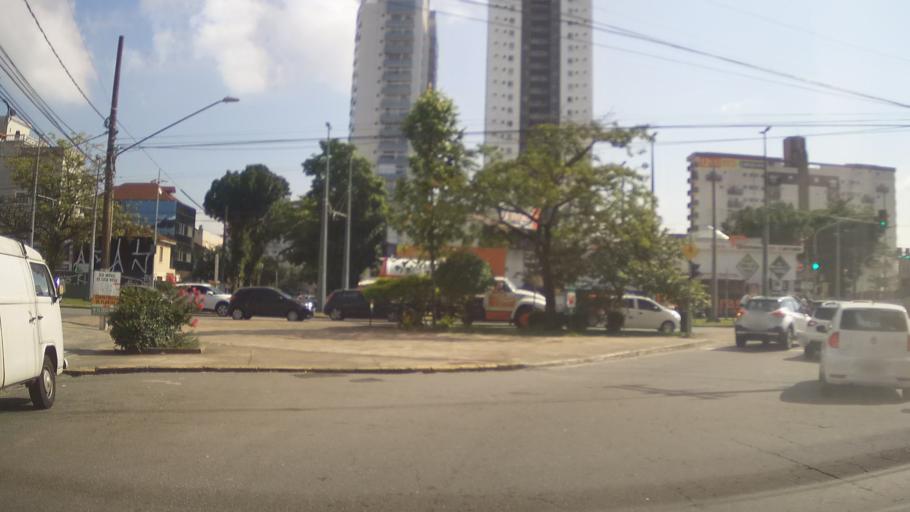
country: BR
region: Sao Paulo
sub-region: Santos
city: Santos
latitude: -23.9583
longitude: -46.3219
